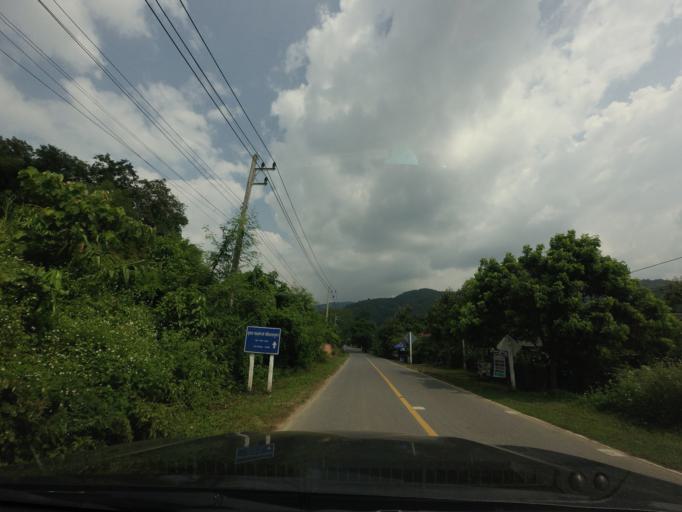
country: TH
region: Nan
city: Pua
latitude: 19.1758
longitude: 100.9532
